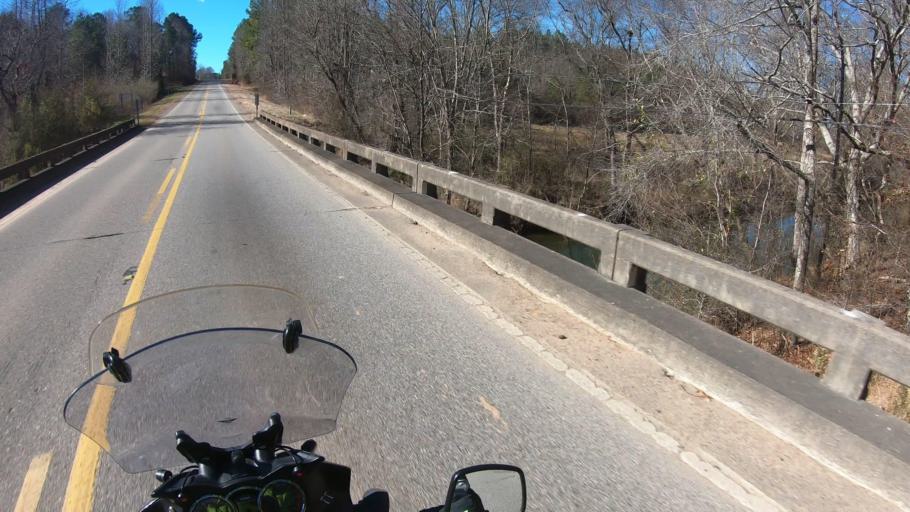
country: US
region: Georgia
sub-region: Haralson County
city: Tallapoosa
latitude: 33.7409
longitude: -85.4053
